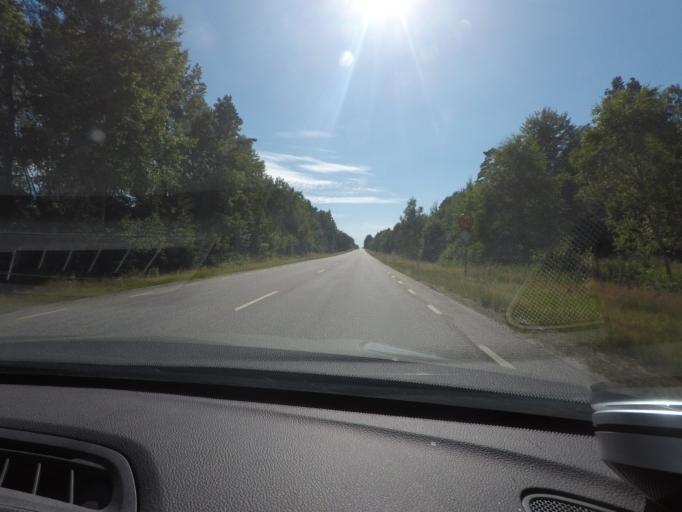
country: SE
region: Kronoberg
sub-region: Markaryds Kommun
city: Markaryd
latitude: 56.4351
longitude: 13.5744
